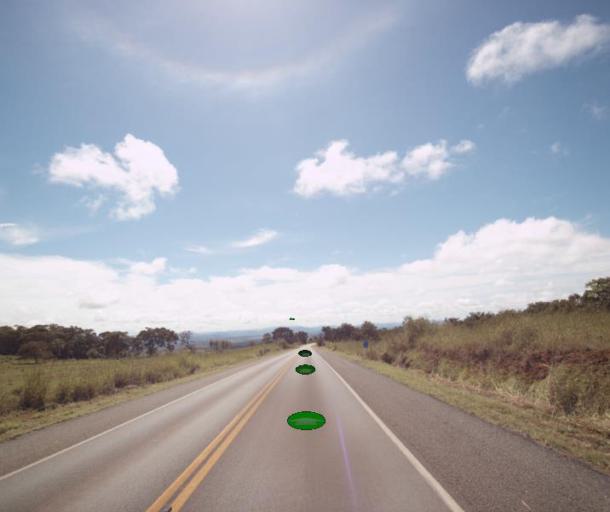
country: BR
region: Goias
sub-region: Padre Bernardo
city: Padre Bernardo
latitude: -15.1822
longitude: -48.4286
